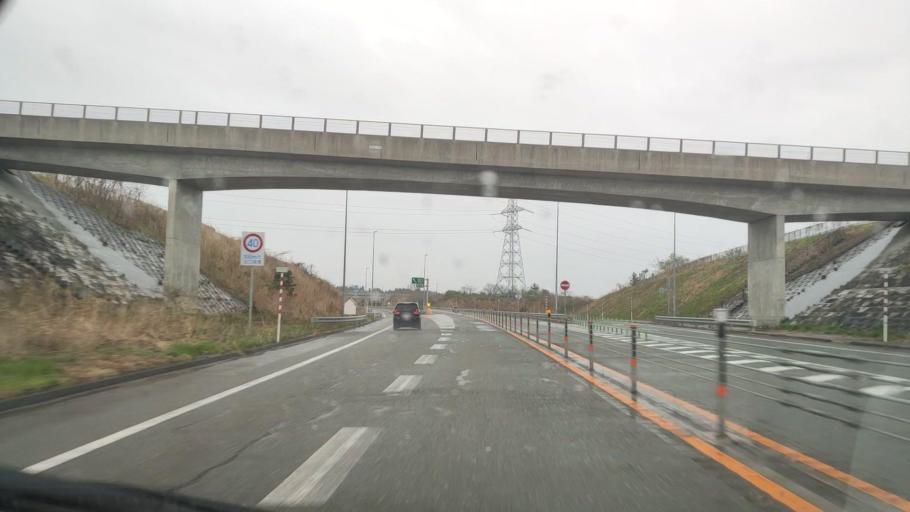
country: JP
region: Akita
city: Noshiromachi
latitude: 40.1561
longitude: 140.0246
